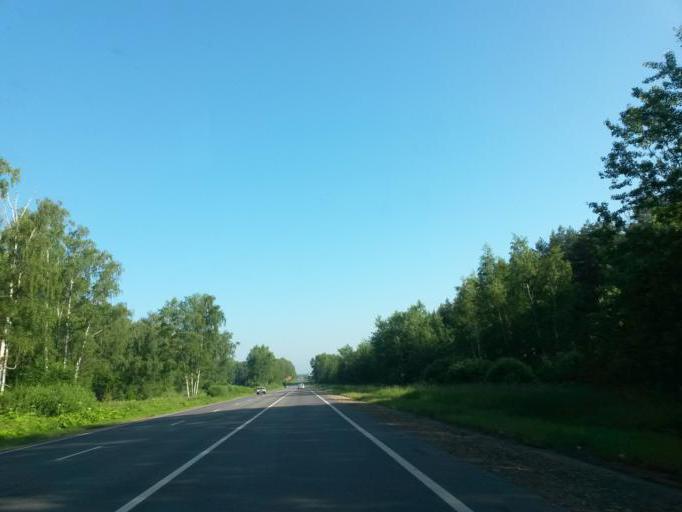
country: RU
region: Moskovskaya
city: Barybino
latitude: 55.2361
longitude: 37.8613
